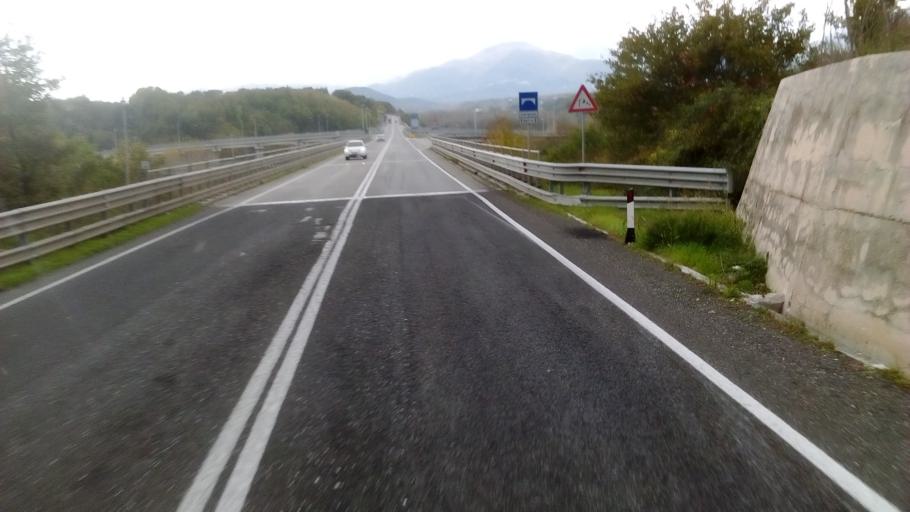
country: IT
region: Molise
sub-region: Provincia di Isernia
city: Isernia
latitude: 41.5804
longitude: 14.2262
